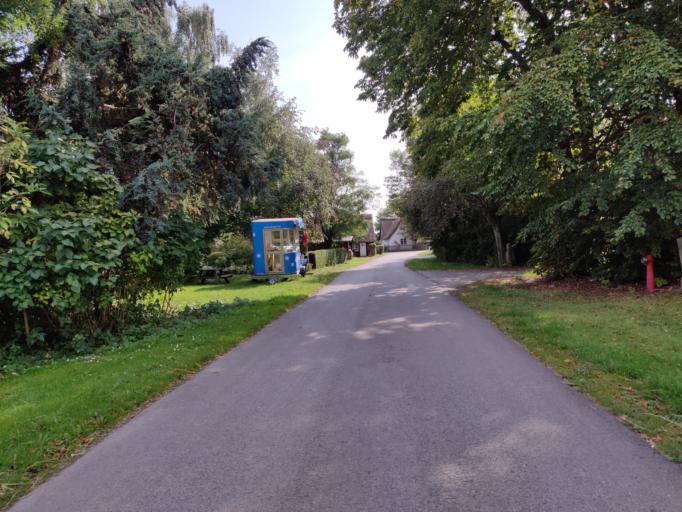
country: DK
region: Zealand
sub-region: Guldborgsund Kommune
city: Nykobing Falster
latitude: 54.6984
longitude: 11.9072
